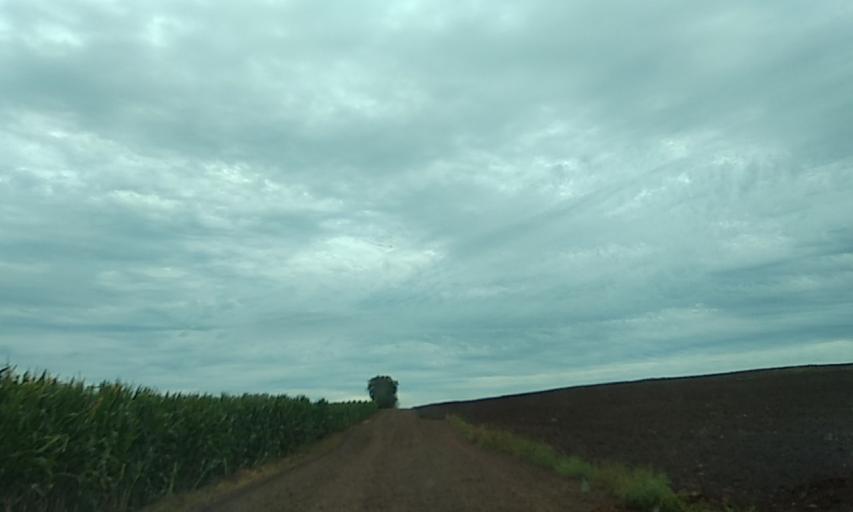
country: BR
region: Parana
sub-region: Marechal Candido Rondon
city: Marechal Candido Rondon
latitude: -24.5276
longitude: -54.0850
